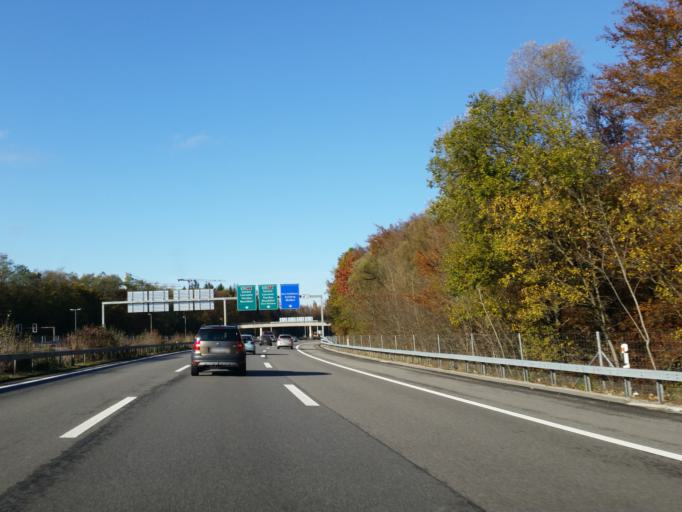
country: CH
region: Bern
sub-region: Bern-Mittelland District
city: Koniz
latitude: 46.9511
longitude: 7.4028
